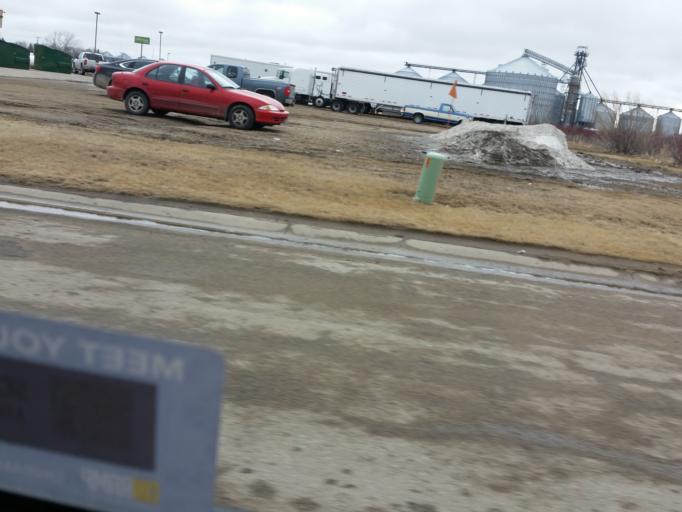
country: US
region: North Dakota
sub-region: Traill County
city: Mayville
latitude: 47.4970
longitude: -97.3130
